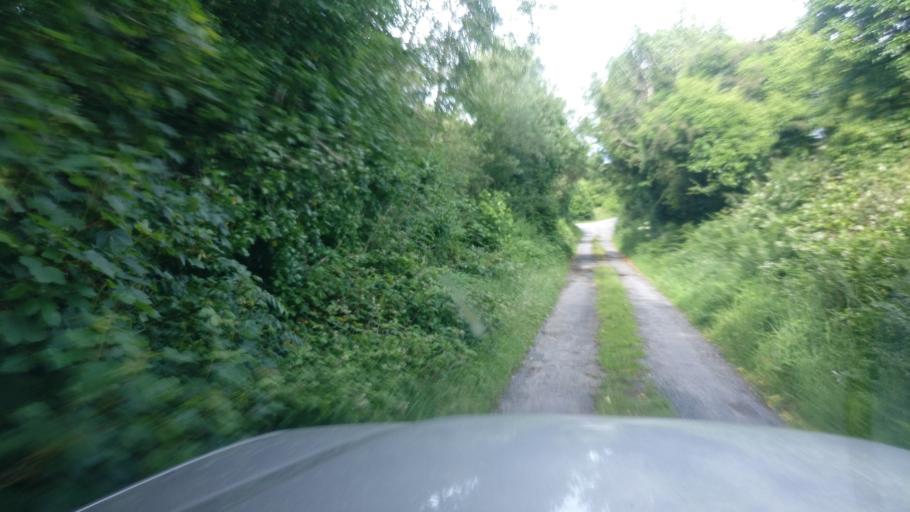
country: IE
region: Connaught
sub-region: County Galway
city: Gort
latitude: 53.1054
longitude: -8.6920
